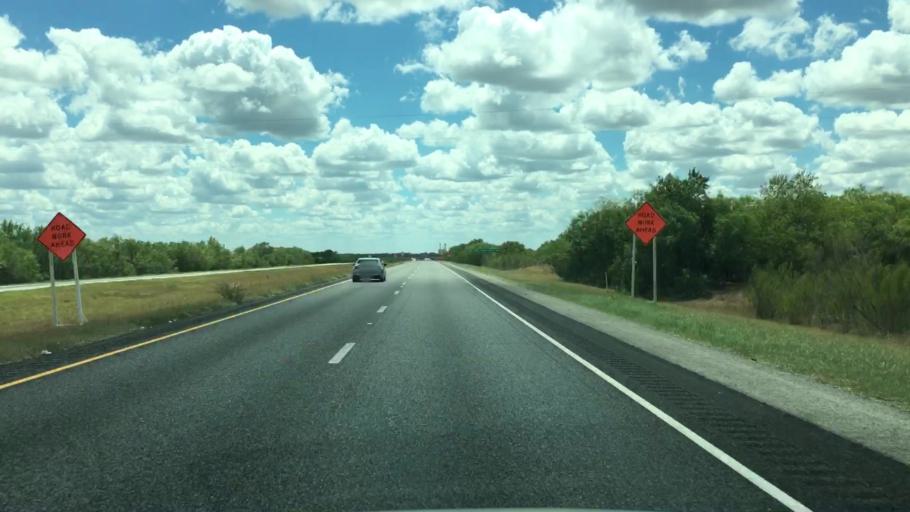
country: US
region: Texas
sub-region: Atascosa County
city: Pleasanton
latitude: 28.9817
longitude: -98.4332
